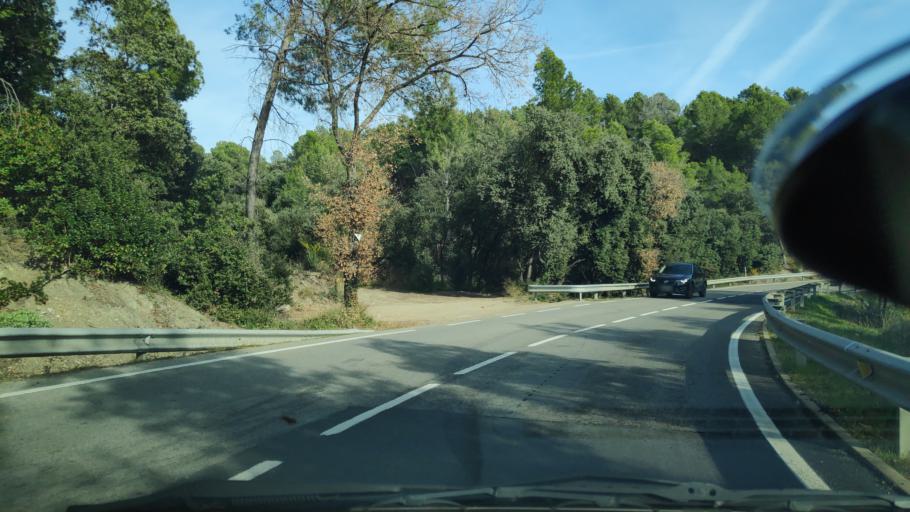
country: ES
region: Catalonia
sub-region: Provincia de Barcelona
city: Matadepera
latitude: 41.5982
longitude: 2.0458
